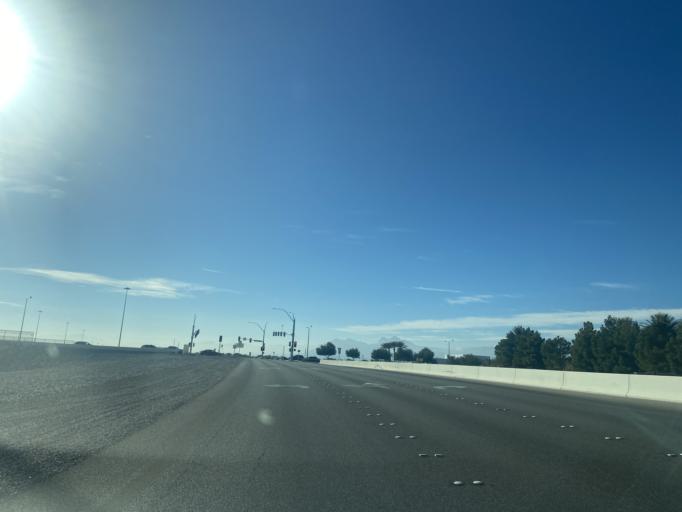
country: US
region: Nevada
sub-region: Clark County
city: North Las Vegas
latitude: 36.2912
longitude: -115.1796
